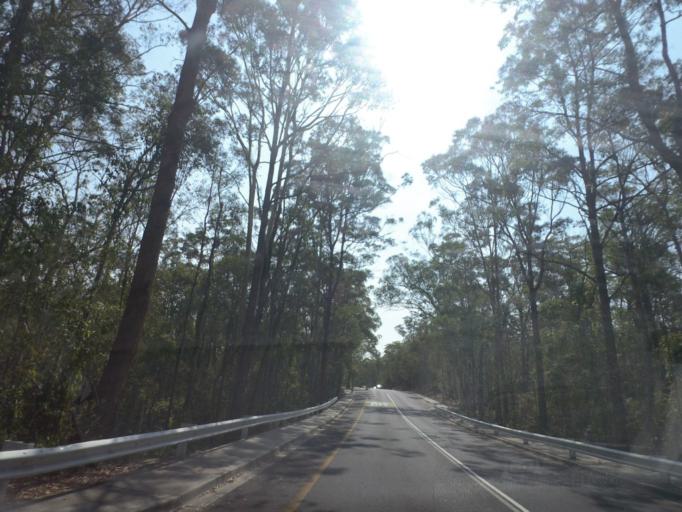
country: AU
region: Queensland
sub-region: Brisbane
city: Nathan
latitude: -27.5505
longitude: 153.0602
